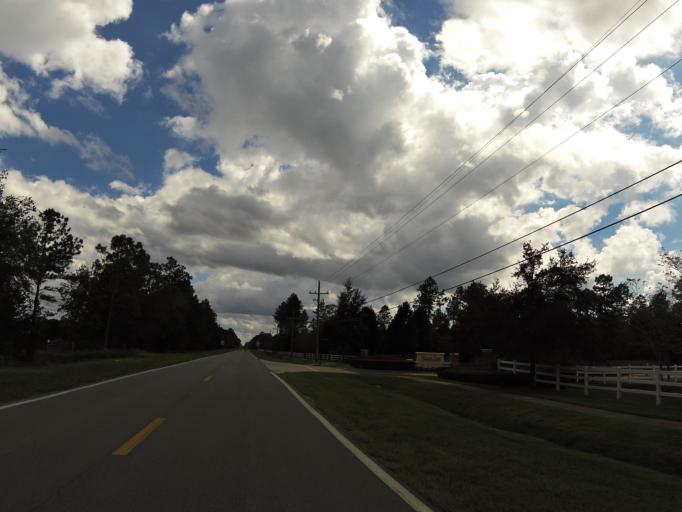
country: US
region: Florida
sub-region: Saint Johns County
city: Saint Augustine
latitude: 29.8965
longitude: -81.4949
